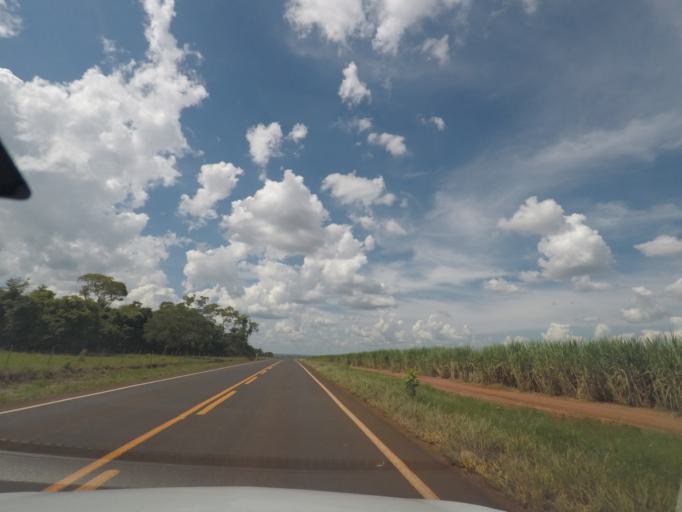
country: BR
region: Minas Gerais
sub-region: Conceicao Das Alagoas
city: Conceicao das Alagoas
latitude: -19.8487
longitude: -48.5969
